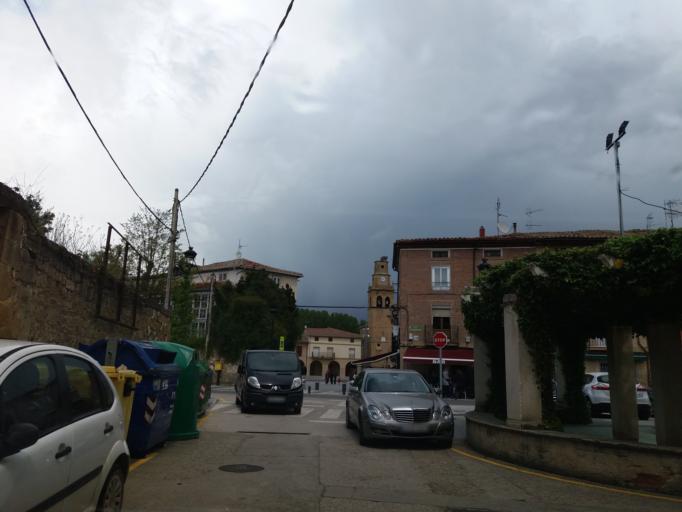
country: ES
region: La Rioja
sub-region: Provincia de La Rioja
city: Anguciana
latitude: 42.5743
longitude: -2.9026
